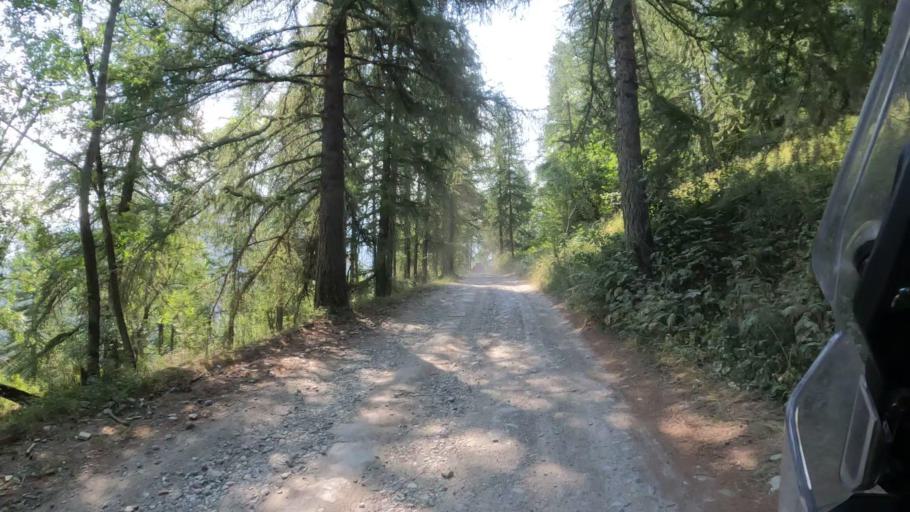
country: IT
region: Piedmont
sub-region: Provincia di Torino
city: Cesana Torinese
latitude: 44.9300
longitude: 6.8126
